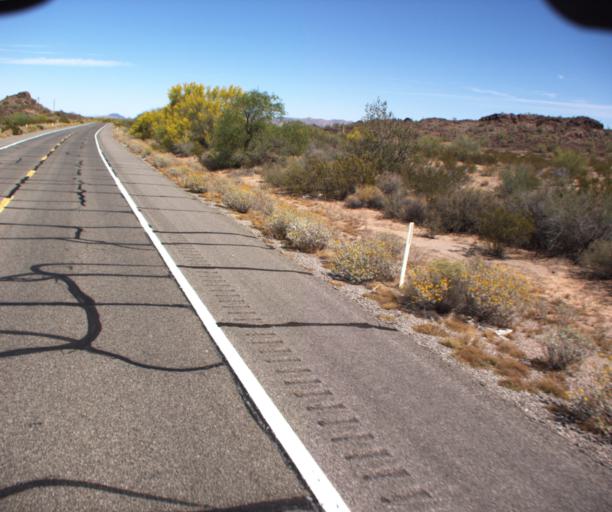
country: US
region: Arizona
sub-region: Pima County
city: Ajo
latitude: 32.5593
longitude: -112.8786
